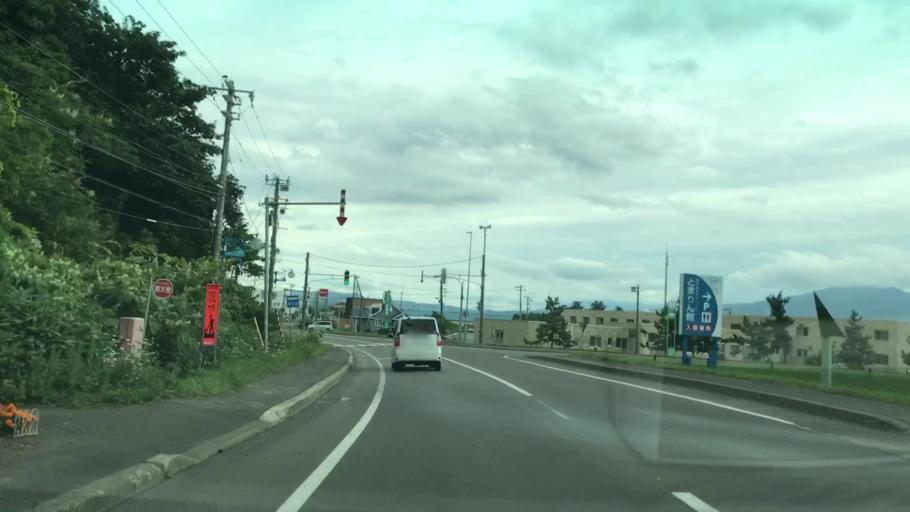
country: JP
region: Hokkaido
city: Iwanai
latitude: 43.0335
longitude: 140.5316
